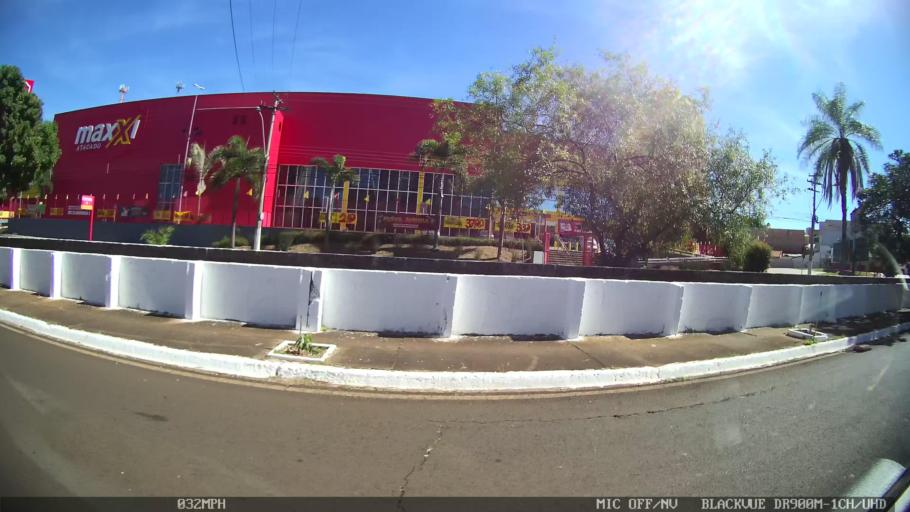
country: BR
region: Sao Paulo
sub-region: Franca
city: Franca
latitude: -20.5497
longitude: -47.4089
